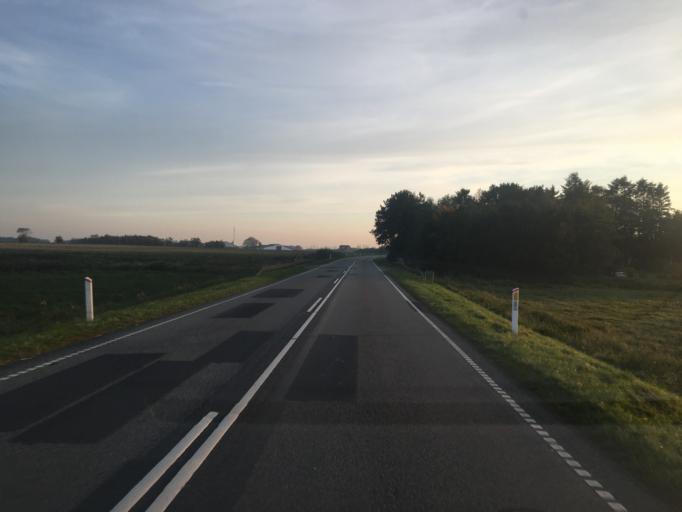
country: DK
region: South Denmark
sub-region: Tonder Kommune
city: Logumkloster
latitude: 55.0480
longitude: 9.0934
